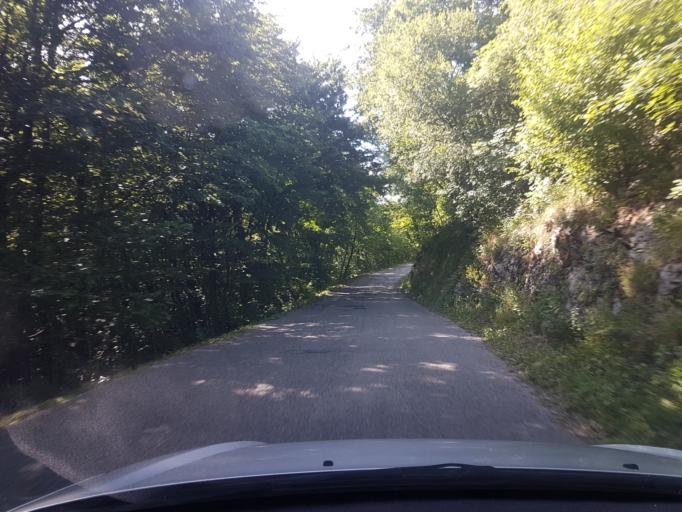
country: SI
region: Divaca
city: Divaca
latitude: 45.7446
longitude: 14.0008
